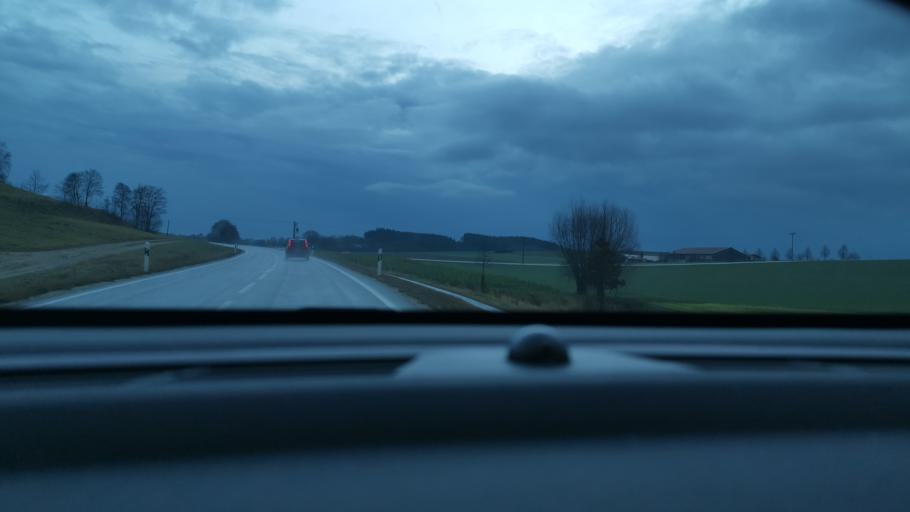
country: DE
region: Bavaria
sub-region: Swabia
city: Petersdorf
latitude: 48.5349
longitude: 11.0147
